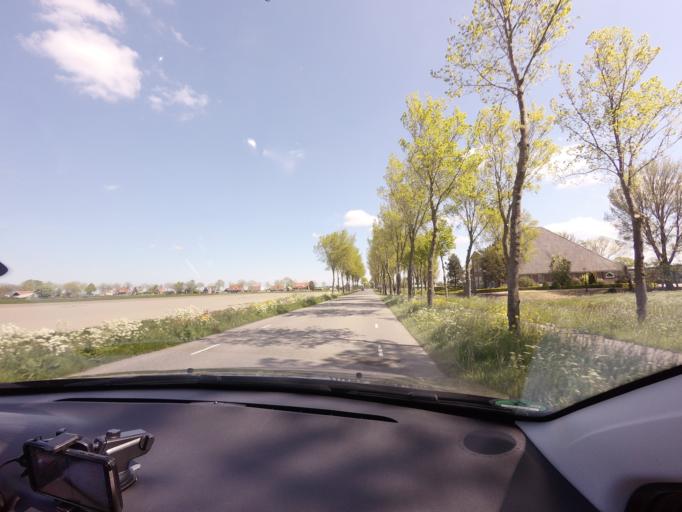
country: NL
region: North Holland
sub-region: Gemeente Beemster
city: Halfweg
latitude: 52.5548
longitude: 4.8839
